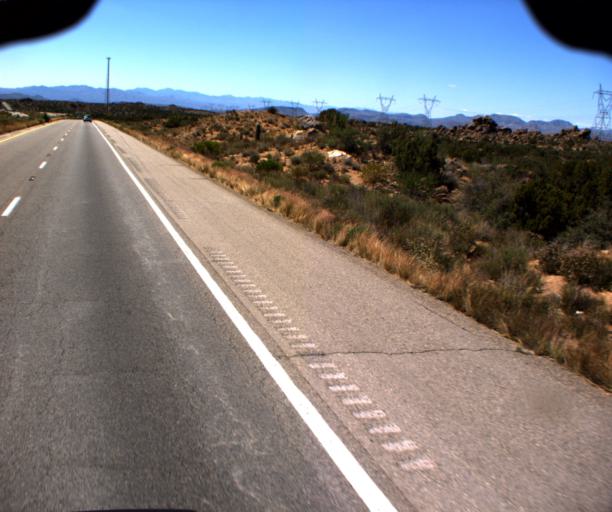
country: US
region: Arizona
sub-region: Yavapai County
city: Bagdad
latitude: 34.4766
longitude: -113.3283
